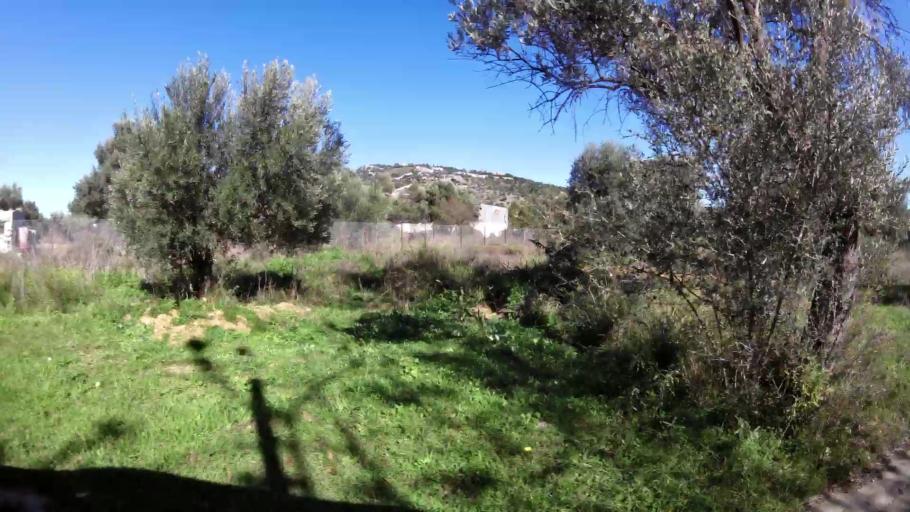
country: GR
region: Attica
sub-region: Nomarchia Anatolikis Attikis
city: Paiania
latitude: 37.9575
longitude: 23.8644
